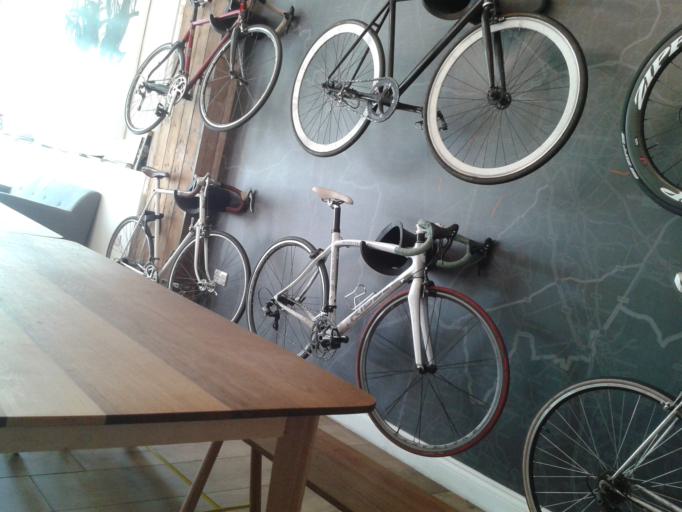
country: GB
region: England
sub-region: Cambridgeshire
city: Cambridge
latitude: 52.2032
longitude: 0.1318
